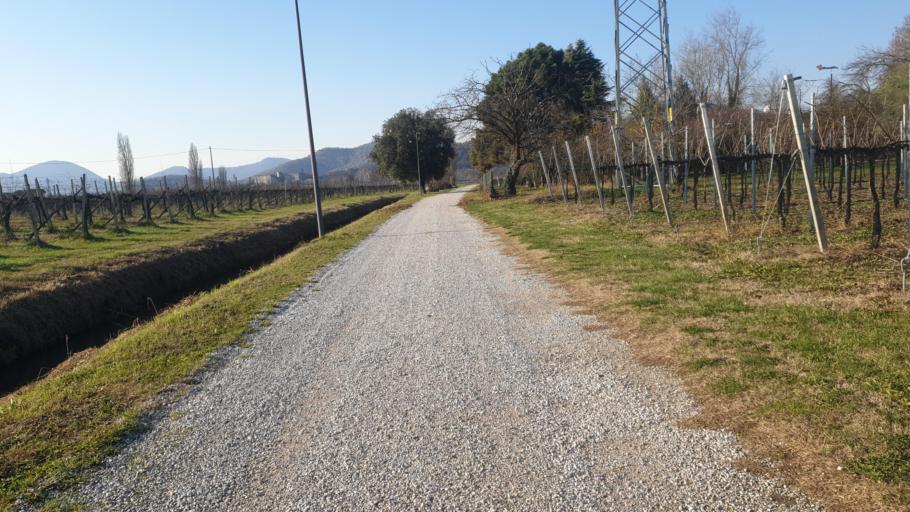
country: IT
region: Veneto
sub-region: Provincia di Padova
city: Carrara San Giorgio
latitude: 45.2973
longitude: 11.8043
